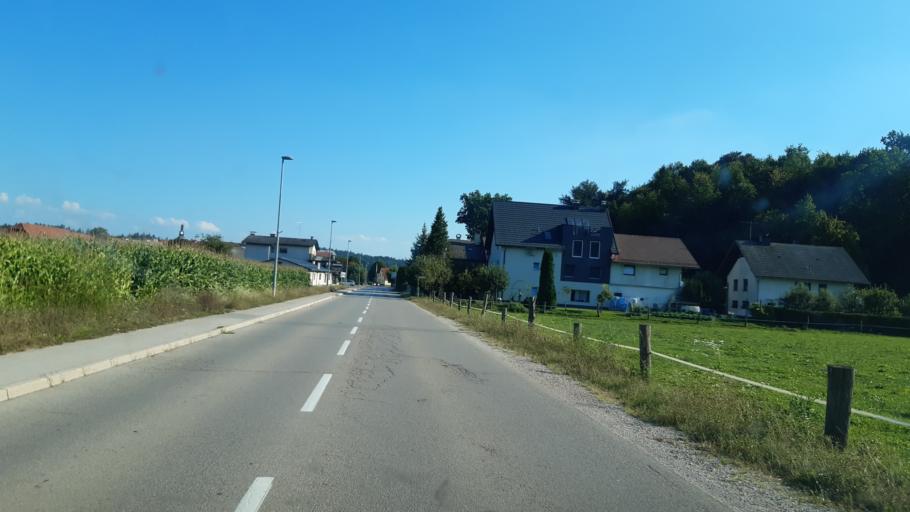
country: SI
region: Ivancna Gorica
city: Ivancna Gorica
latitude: 45.9423
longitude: 14.8038
